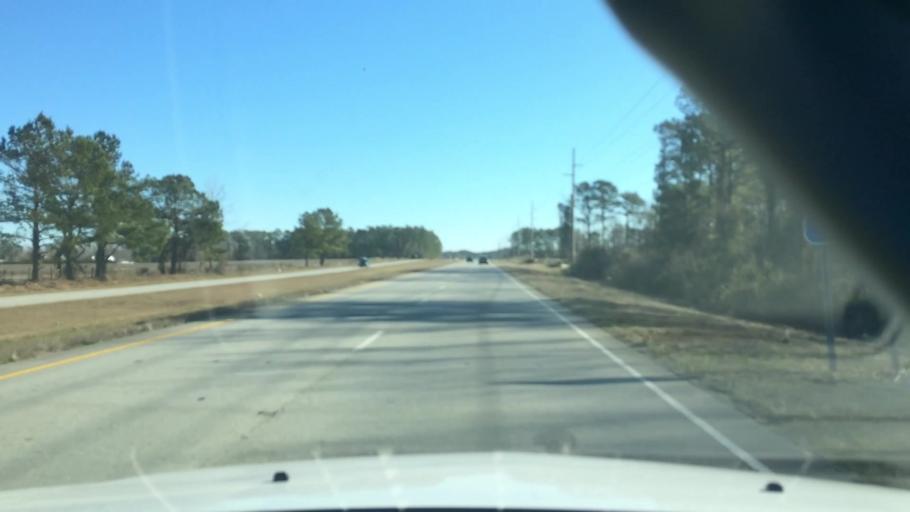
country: US
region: North Carolina
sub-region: Brunswick County
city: Shallotte
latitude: 33.9551
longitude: -78.4447
